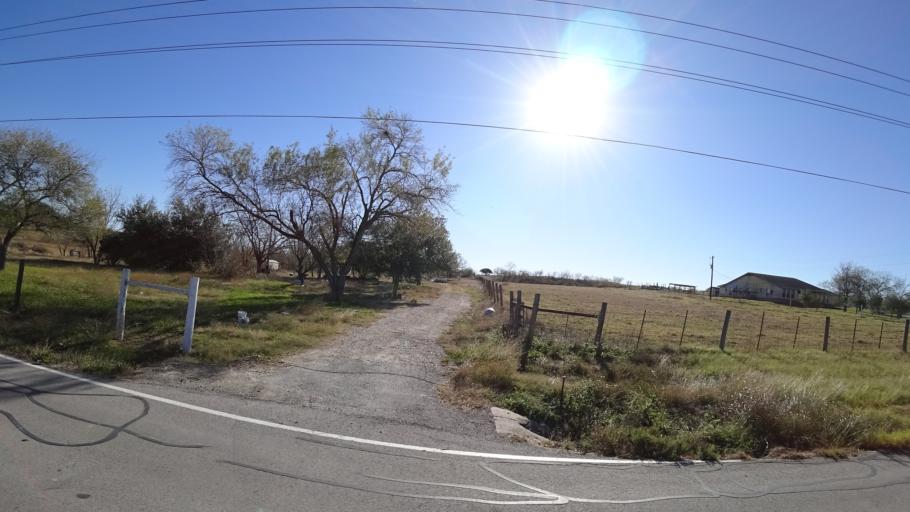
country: US
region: Texas
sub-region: Travis County
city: Onion Creek
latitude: 30.1091
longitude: -97.6721
